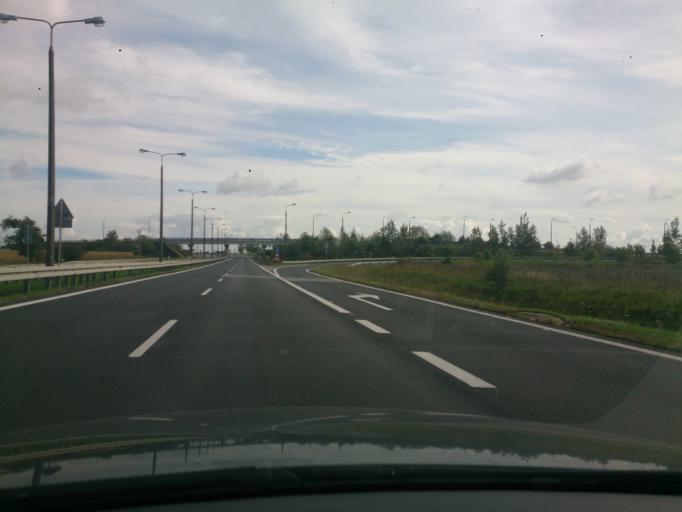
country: PL
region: Kujawsko-Pomorskie
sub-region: Powiat swiecki
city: Swiecie
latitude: 53.4200
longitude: 18.4761
